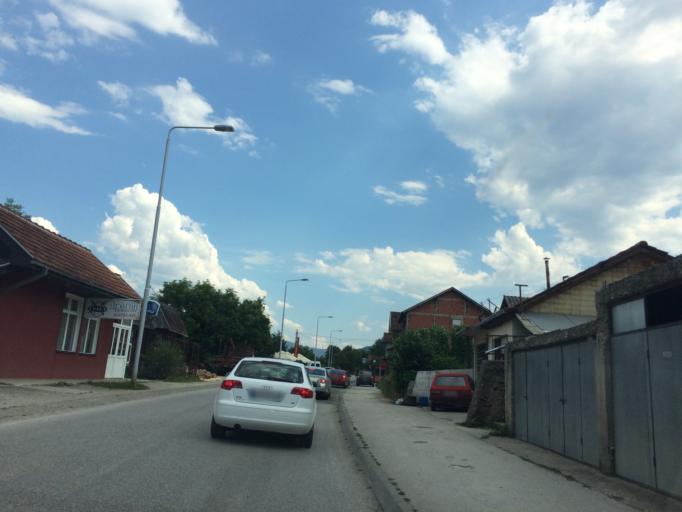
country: RS
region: Central Serbia
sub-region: Zlatiborski Okrug
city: Prijepolje
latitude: 43.3637
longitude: 19.6315
